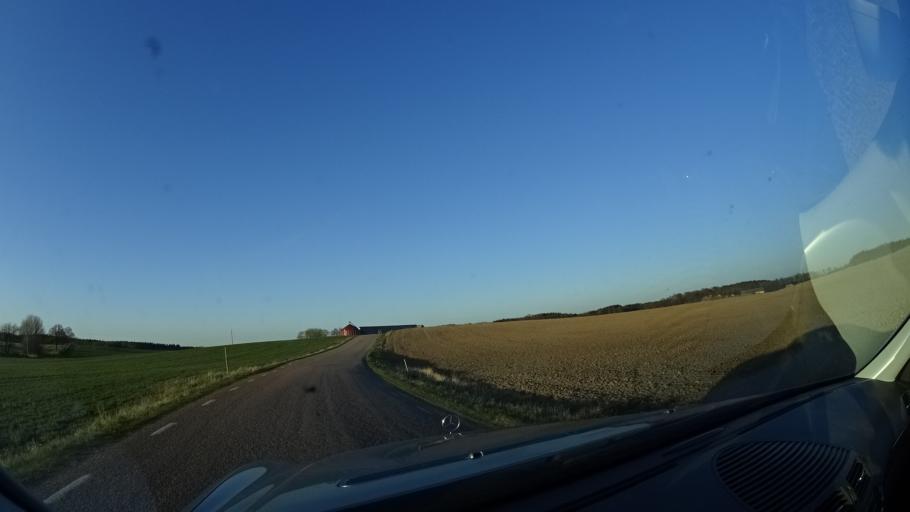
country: SE
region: Skane
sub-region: Eslovs Kommun
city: Stehag
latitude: 55.9463
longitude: 13.2971
